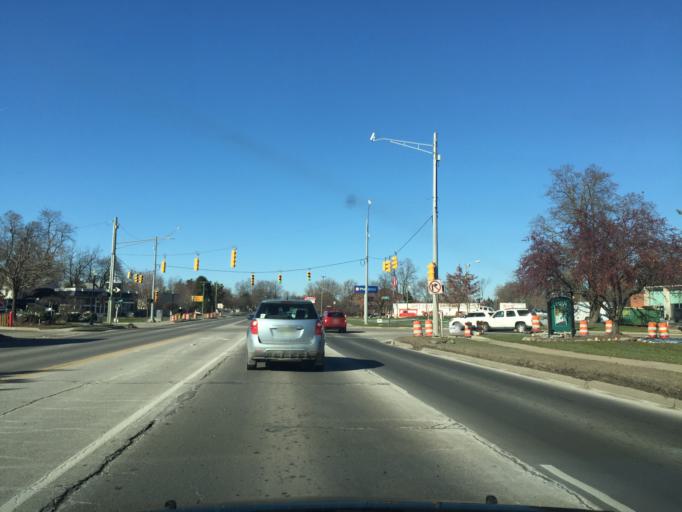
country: US
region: Michigan
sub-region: Oakland County
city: Lake Orion
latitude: 42.7842
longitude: -83.2416
